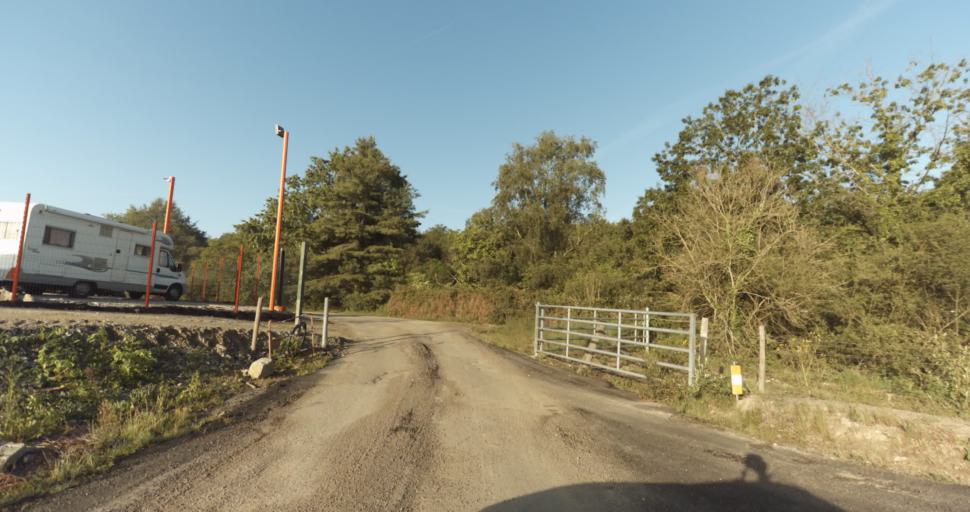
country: FR
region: Limousin
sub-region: Departement de la Haute-Vienne
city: Condat-sur-Vienne
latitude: 45.7848
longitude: 1.3037
